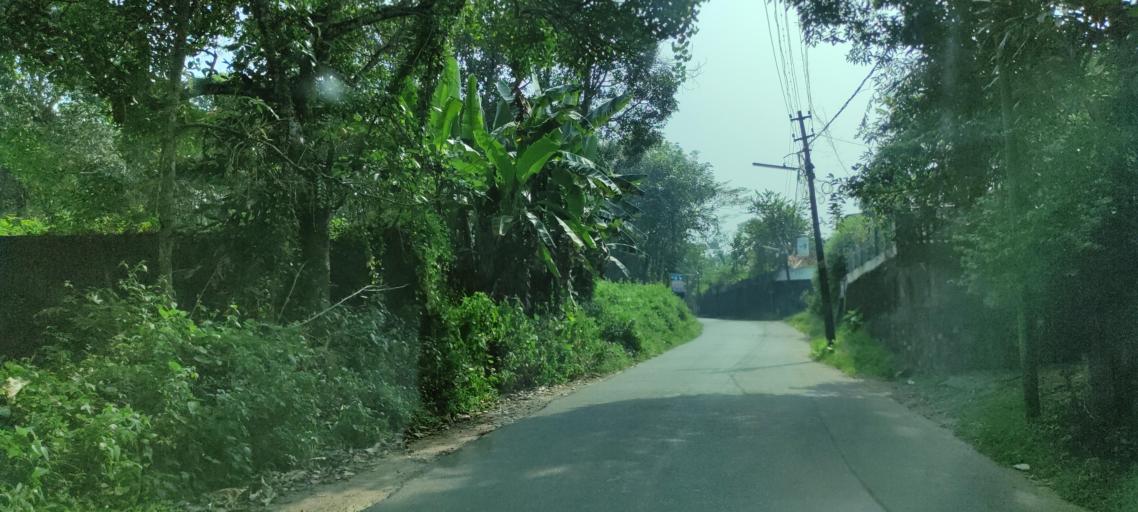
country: IN
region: Kerala
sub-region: Pattanamtitta
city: Adur
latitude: 9.2250
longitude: 76.7135
